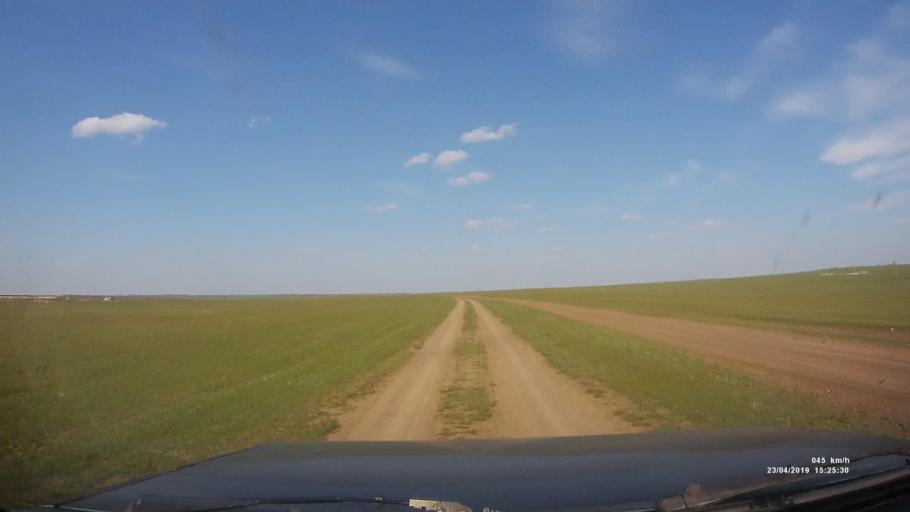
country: RU
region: Rostov
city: Remontnoye
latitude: 46.5417
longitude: 42.9817
